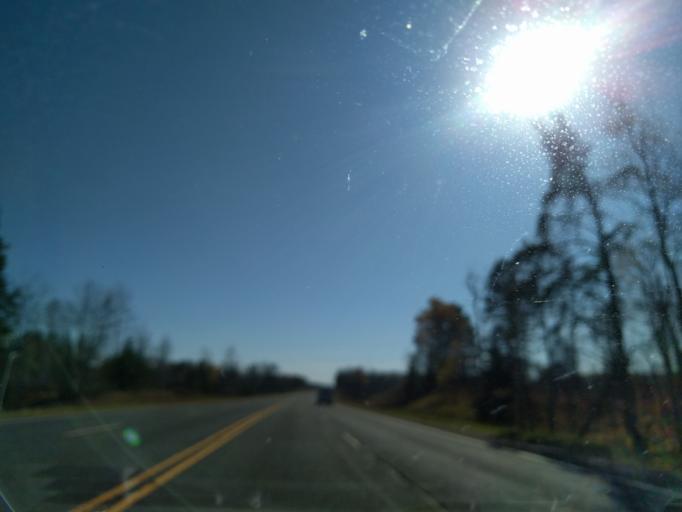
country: US
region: Michigan
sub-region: Iron County
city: Crystal Falls
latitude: 46.2393
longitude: -88.0083
